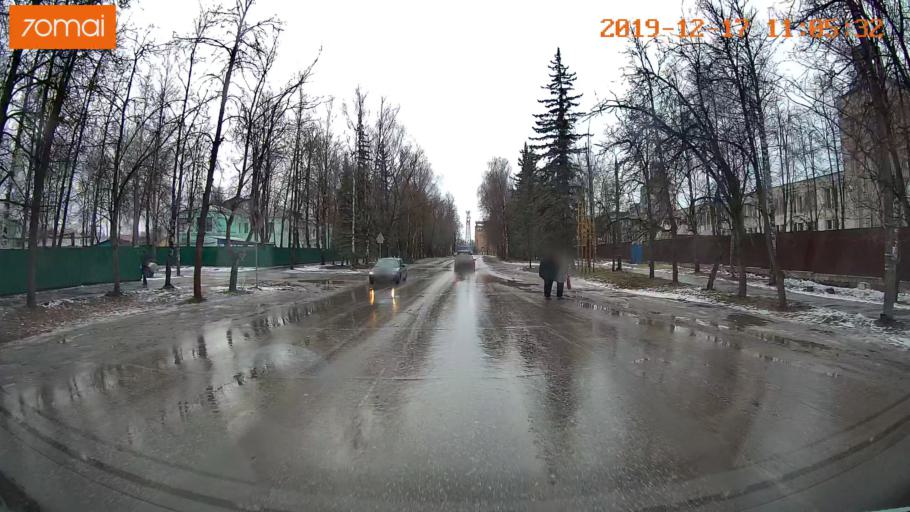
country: RU
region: Vladimir
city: Gus'-Khrustal'nyy
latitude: 55.6205
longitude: 40.6430
